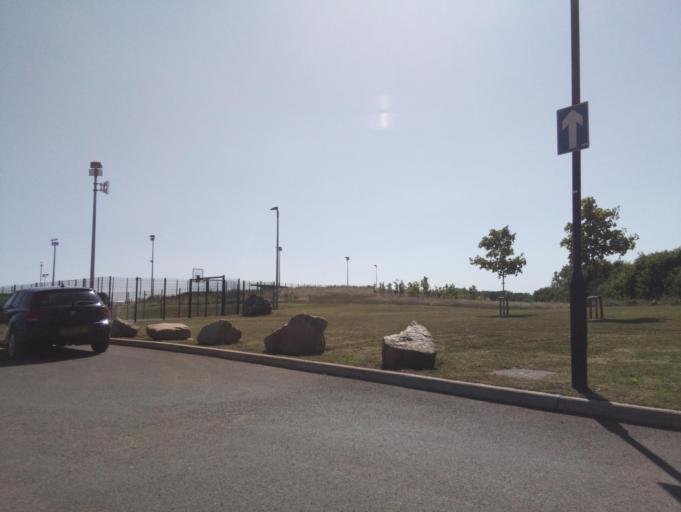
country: GB
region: England
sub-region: Borough of Torbay
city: Paignton
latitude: 50.4124
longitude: -3.5850
